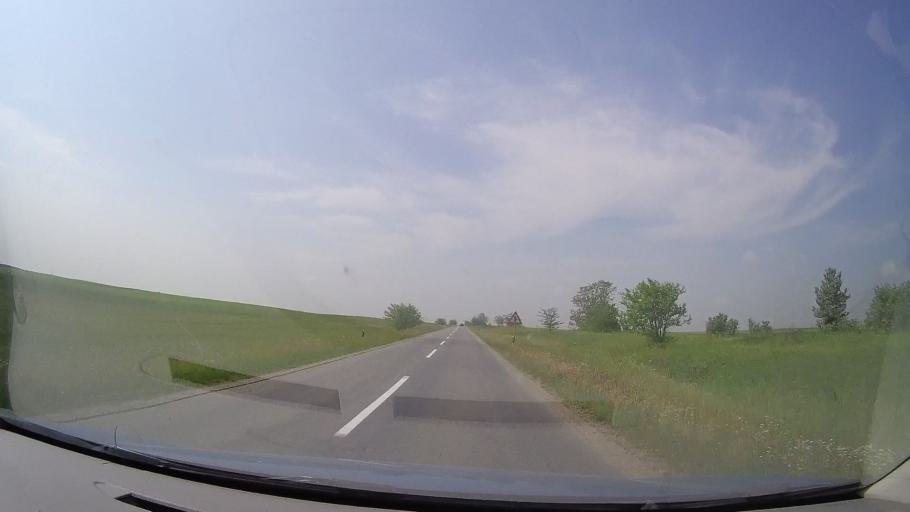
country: RS
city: Samos
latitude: 45.1684
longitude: 20.7542
